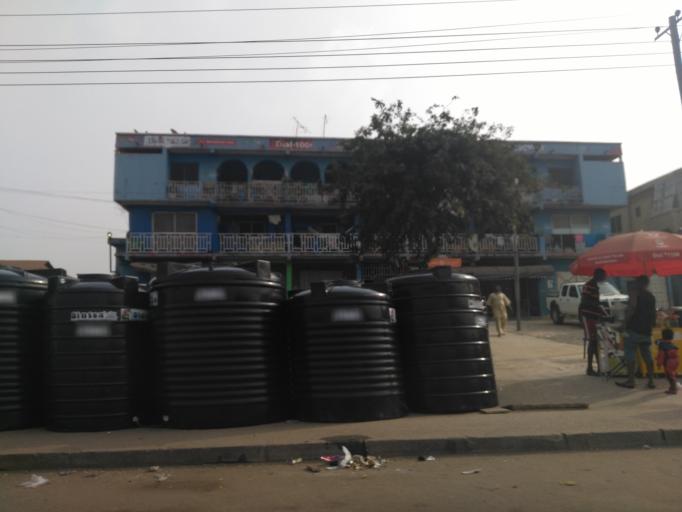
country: GH
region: Ashanti
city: Kumasi
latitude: 6.6987
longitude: -1.5945
